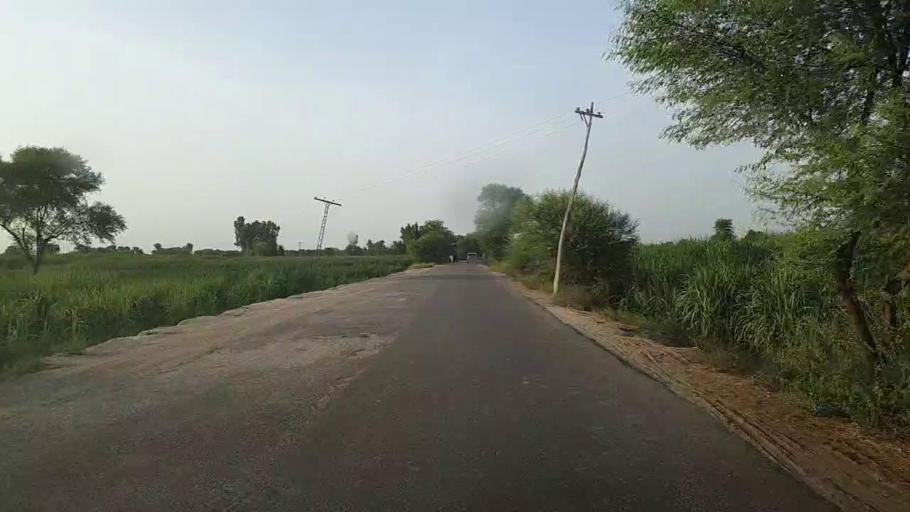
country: PK
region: Sindh
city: Ubauro
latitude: 28.1746
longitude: 69.8291
